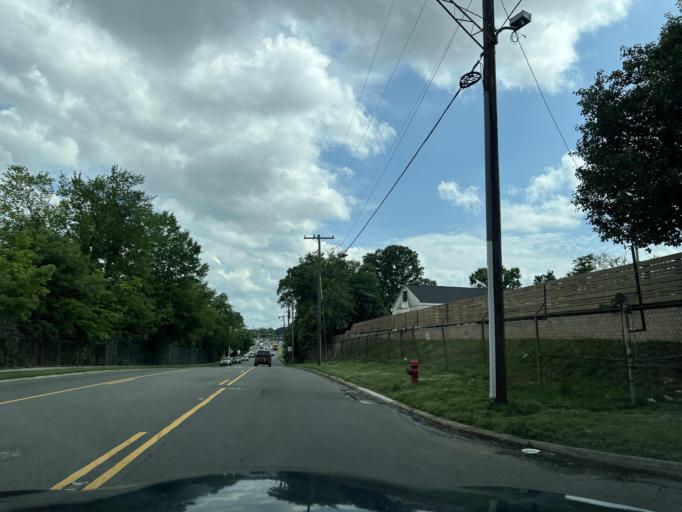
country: US
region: North Carolina
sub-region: Durham County
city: Durham
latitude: 35.9972
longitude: -78.8860
